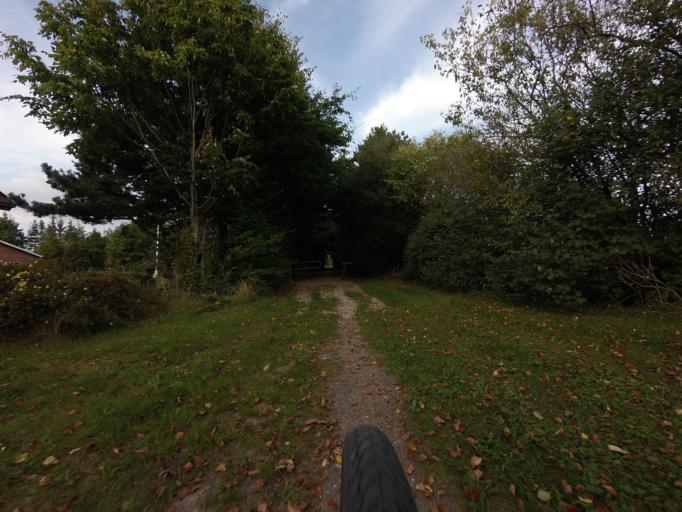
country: DK
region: Central Jutland
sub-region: Ikast-Brande Kommune
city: Brande
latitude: 55.9023
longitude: 9.0783
